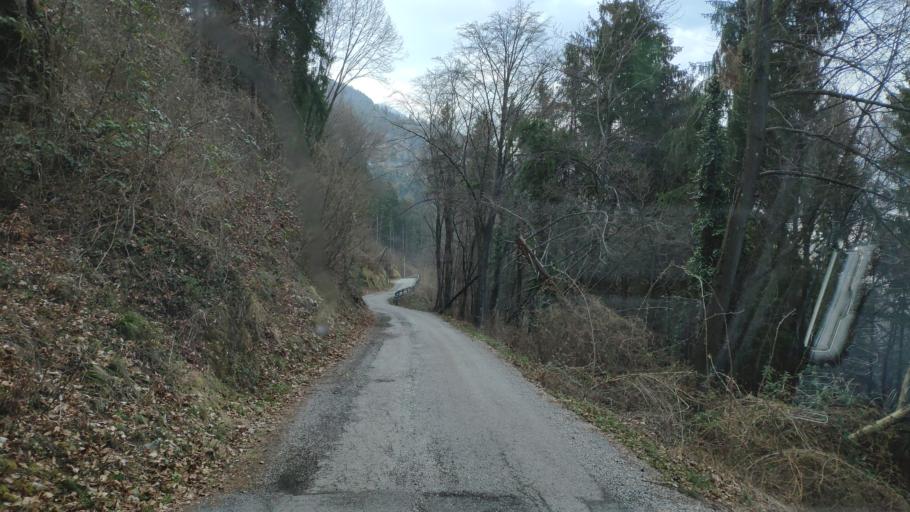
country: IT
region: Veneto
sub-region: Provincia di Vicenza
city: Enego
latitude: 45.9504
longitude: 11.7088
